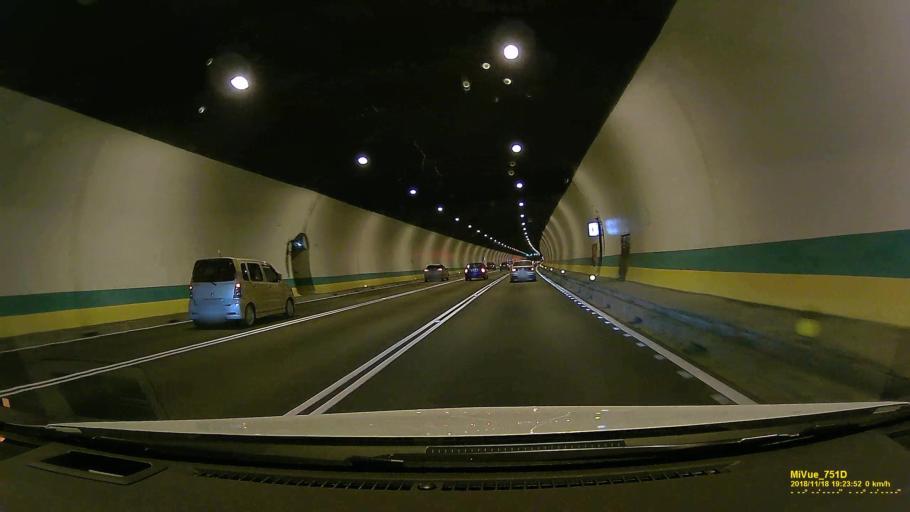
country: TW
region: Taipei
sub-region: Taipei
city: Banqiao
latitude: 24.9817
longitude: 121.4957
